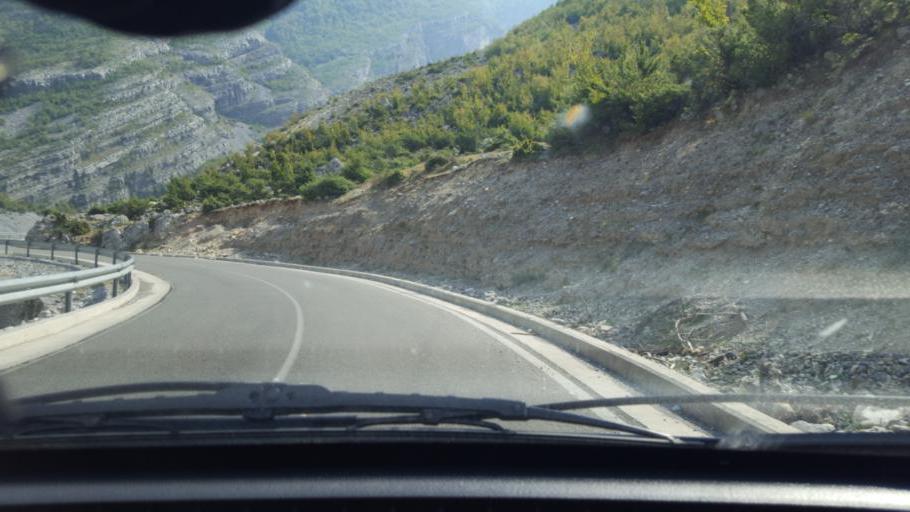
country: AL
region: Shkoder
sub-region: Rrethi i Malesia e Madhe
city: Kastrat
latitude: 42.4914
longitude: 19.5806
